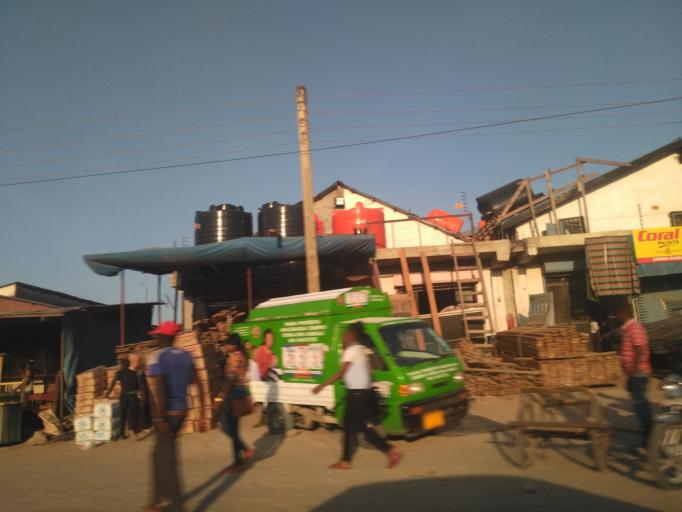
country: TZ
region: Pwani
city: Vikindu
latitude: -6.9256
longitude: 39.2714
